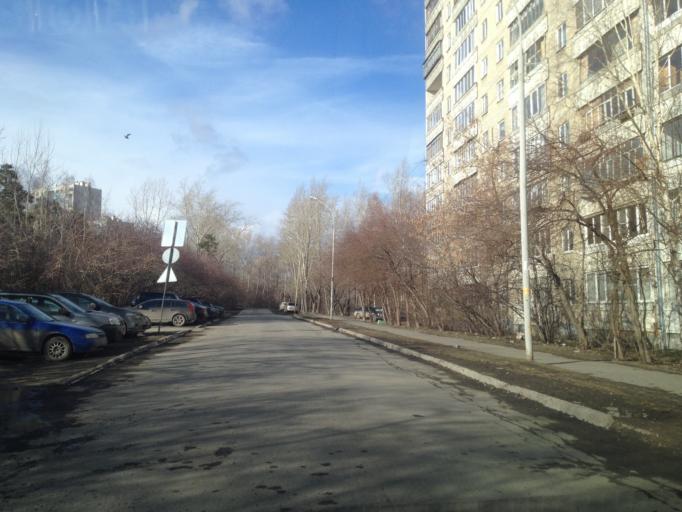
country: RU
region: Sverdlovsk
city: Sovkhoznyy
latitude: 56.7627
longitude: 60.6081
